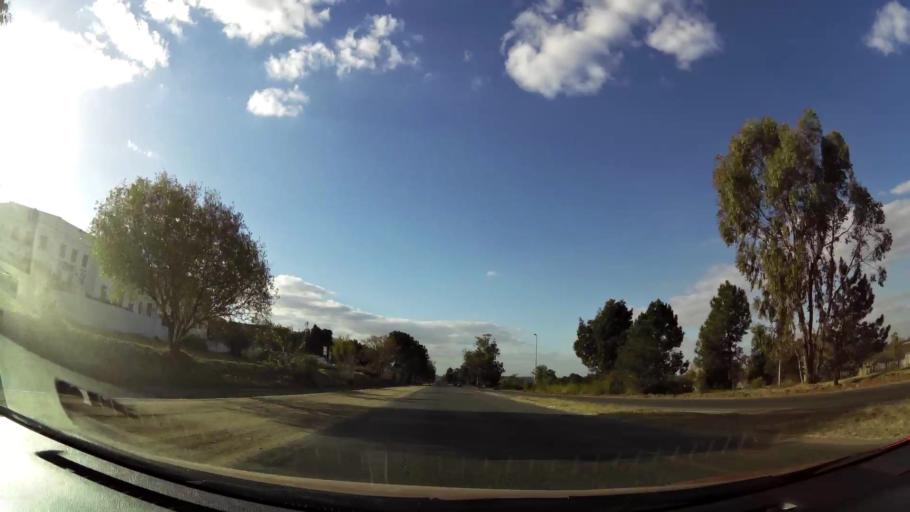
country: ZA
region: Gauteng
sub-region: City of Johannesburg Metropolitan Municipality
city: Midrand
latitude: -25.9774
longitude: 28.1342
